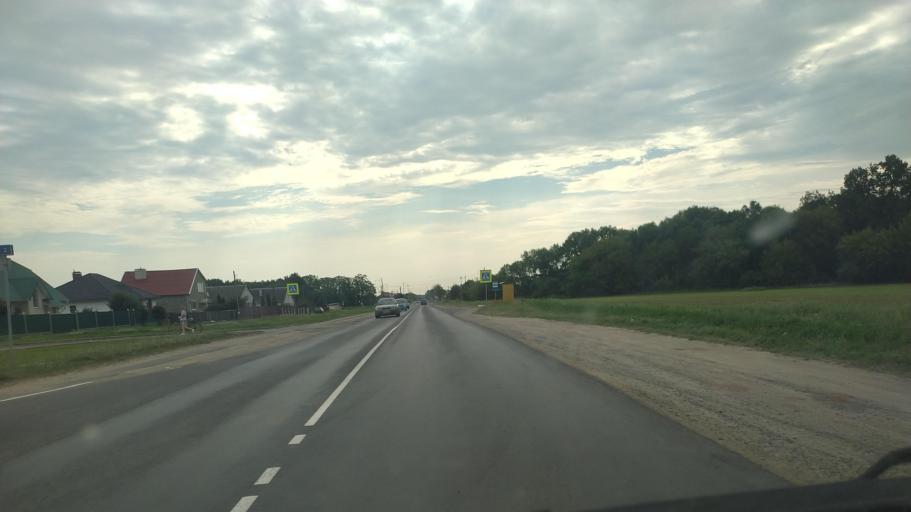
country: BY
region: Brest
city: Byaroza
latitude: 52.5463
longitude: 24.9563
